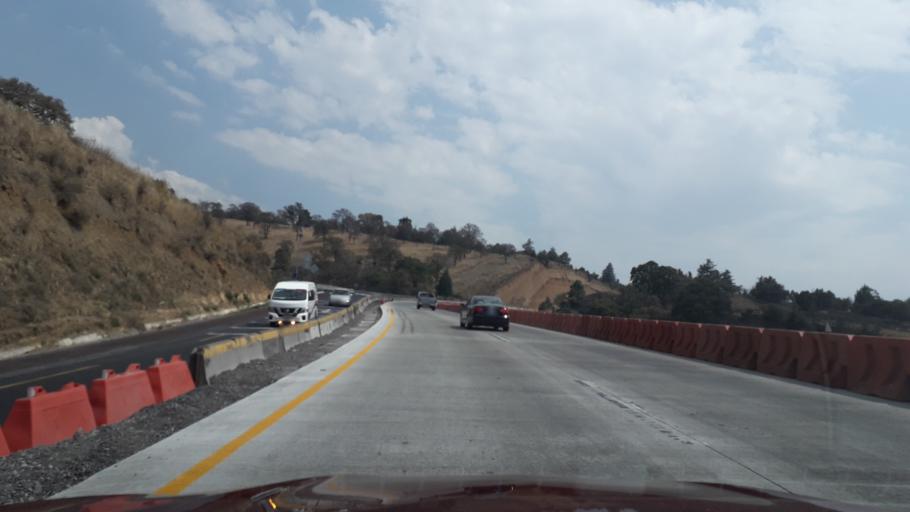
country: MX
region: Mexico
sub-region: Ixtapaluca
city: San Jeronimo Cuatro Vientos
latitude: 19.3123
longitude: -98.7937
